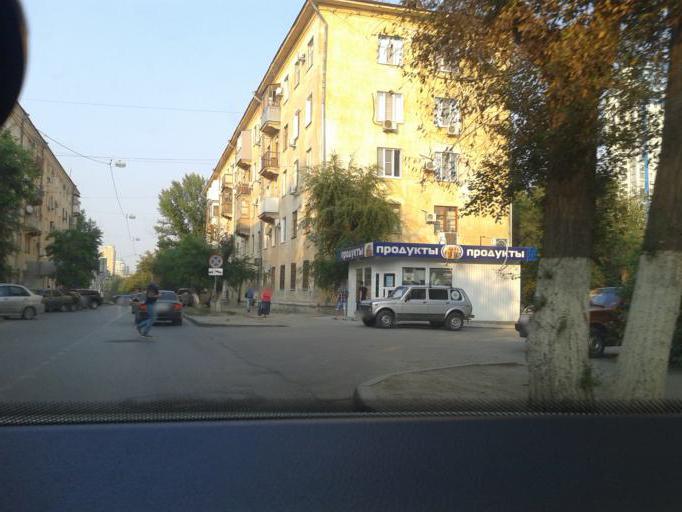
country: RU
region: Volgograd
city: Volgograd
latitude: 48.6981
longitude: 44.5065
